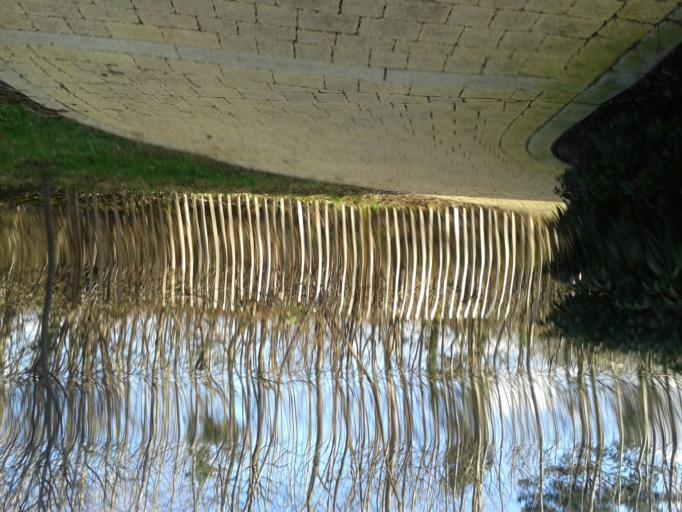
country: GB
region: England
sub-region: Cambridgeshire
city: Grantchester
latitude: 52.1695
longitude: 0.1176
